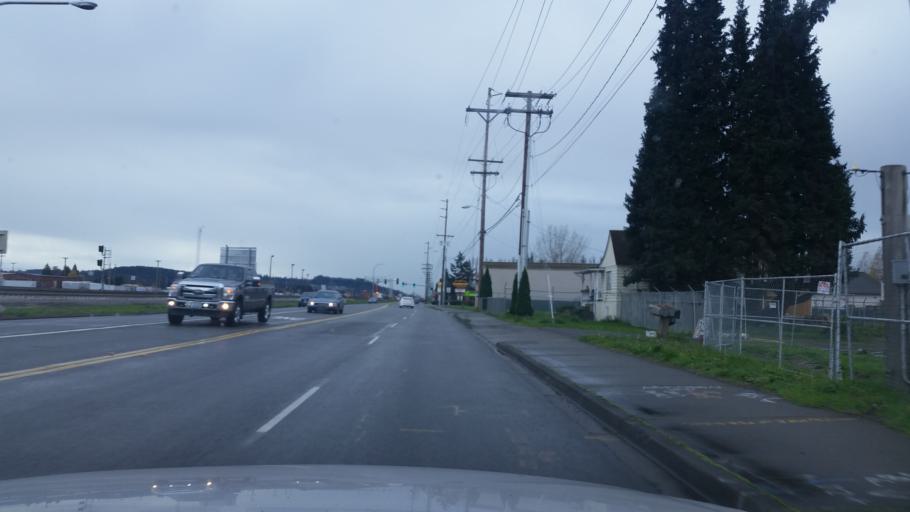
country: US
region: Washington
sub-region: King County
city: Auburn
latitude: 47.3029
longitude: -122.2326
